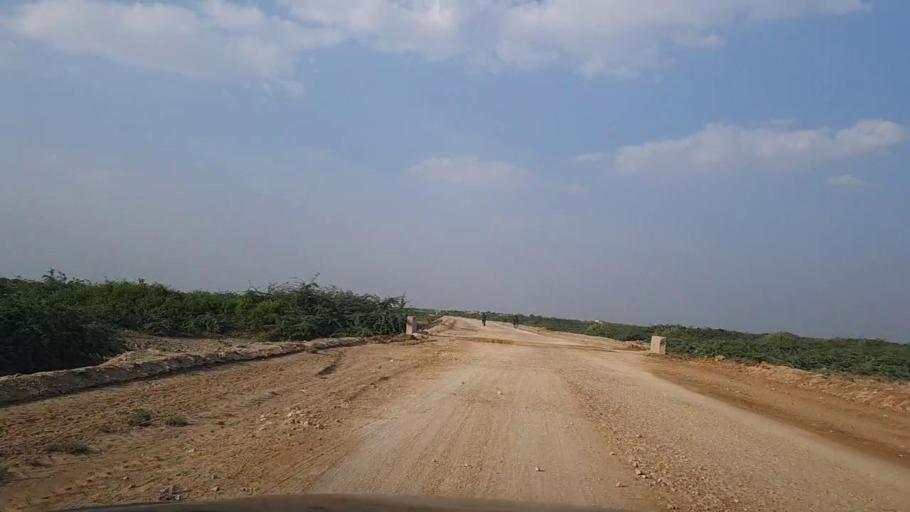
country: PK
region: Sindh
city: Gharo
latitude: 24.7939
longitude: 67.7448
